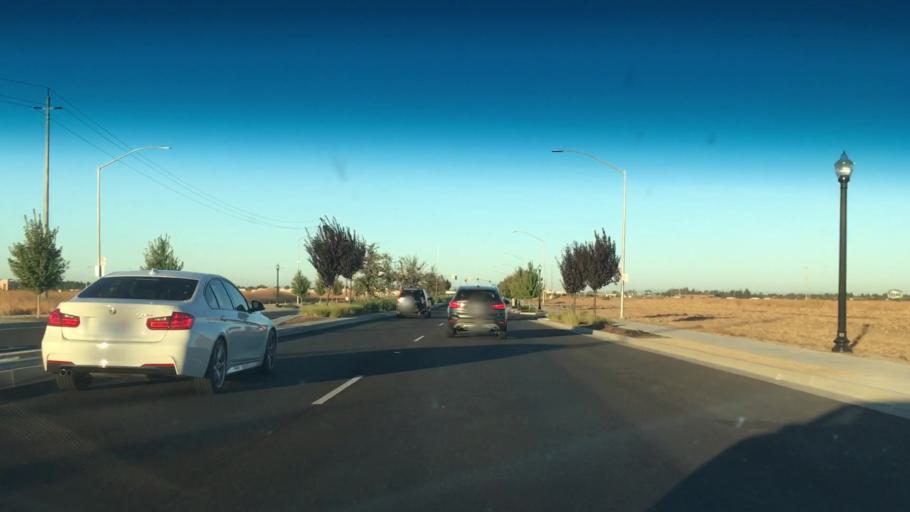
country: US
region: California
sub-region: Sacramento County
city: Parkway
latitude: 38.4642
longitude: -121.4743
